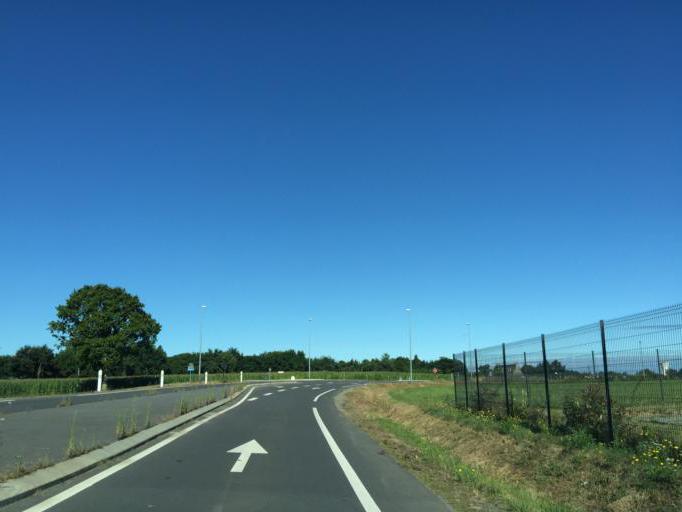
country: FR
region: Brittany
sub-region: Departement des Cotes-d'Armor
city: Pleslin-Trigavou
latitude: 48.5216
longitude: -2.0435
